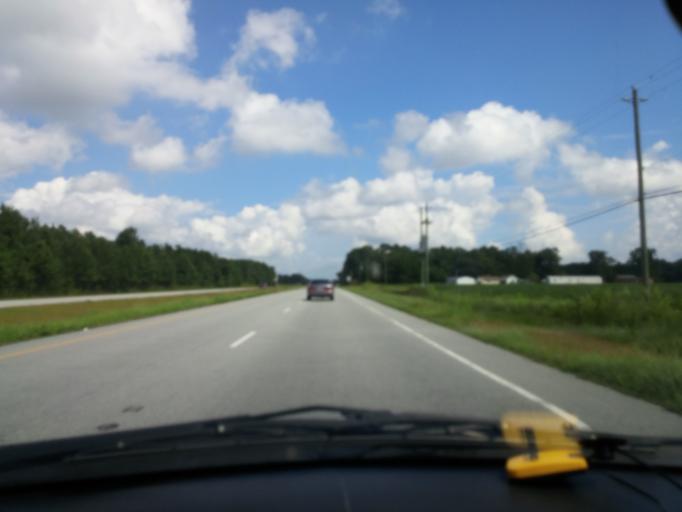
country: US
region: North Carolina
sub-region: Duplin County
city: Beulaville
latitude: 35.1123
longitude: -77.7179
